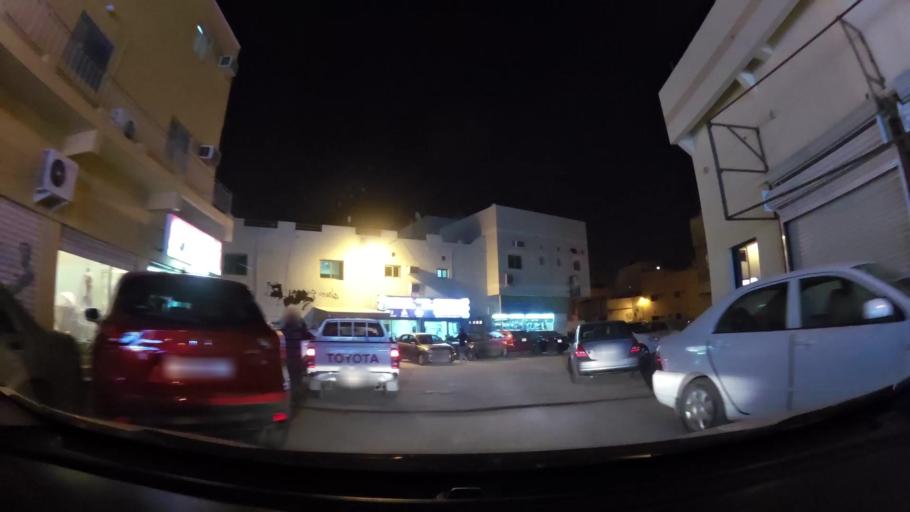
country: BH
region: Manama
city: Jidd Hafs
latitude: 26.2195
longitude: 50.5382
